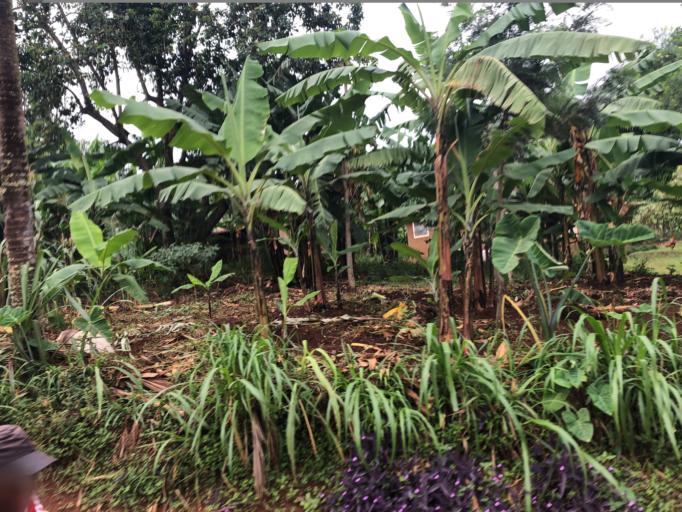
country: UG
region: Central Region
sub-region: Mukono District
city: Mukono
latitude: 0.3595
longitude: 32.7460
